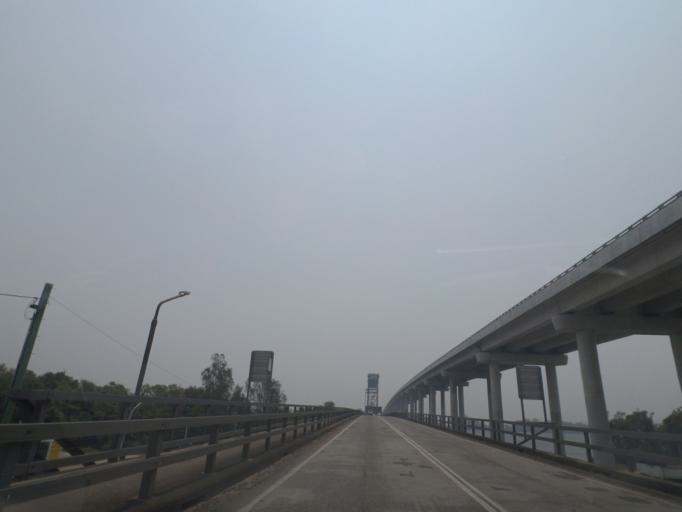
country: AU
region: New South Wales
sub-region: Clarence Valley
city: Maclean
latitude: -29.4336
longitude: 153.2407
